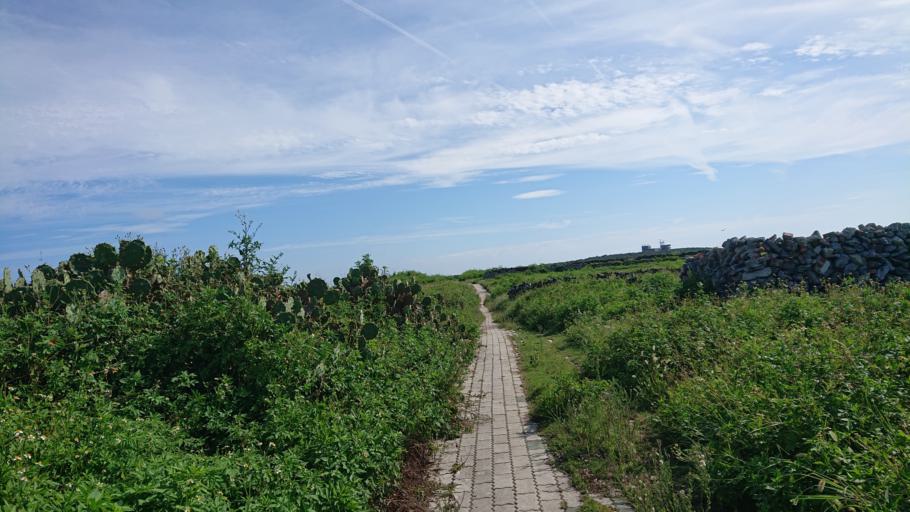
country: TW
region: Taiwan
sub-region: Penghu
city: Ma-kung
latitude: 23.6524
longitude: 119.5225
